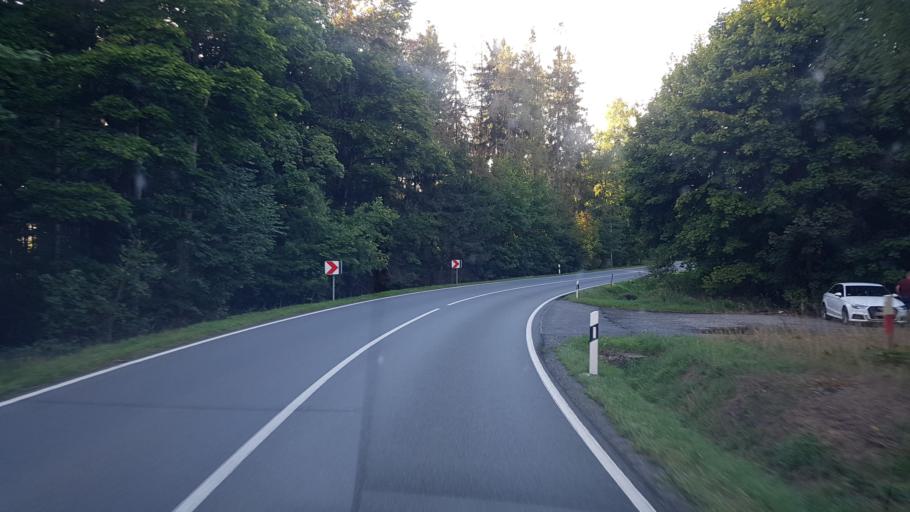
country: DE
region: Thuringia
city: Birkenhugel
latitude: 50.4461
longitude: 11.7123
